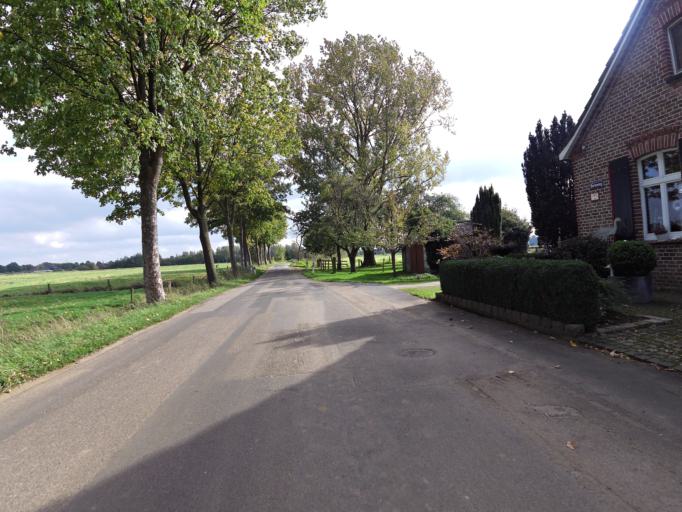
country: DE
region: North Rhine-Westphalia
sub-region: Regierungsbezirk Munster
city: Isselburg
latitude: 51.8248
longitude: 6.4789
